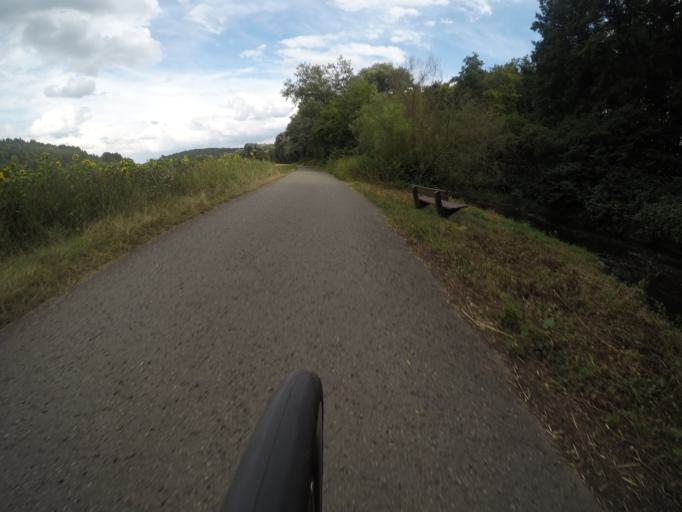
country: DE
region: Baden-Wuerttemberg
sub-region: Regierungsbezirk Stuttgart
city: Weil der Stadt
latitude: 48.7621
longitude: 8.8662
